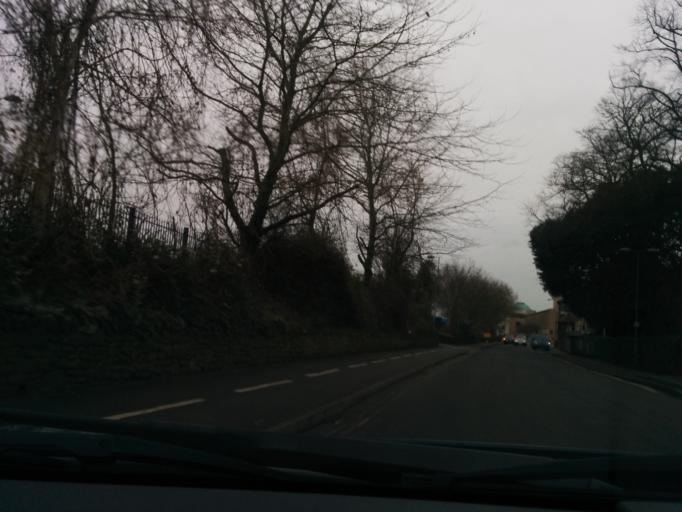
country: GB
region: England
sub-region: Oxfordshire
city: Oxford
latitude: 51.7513
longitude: -1.2689
